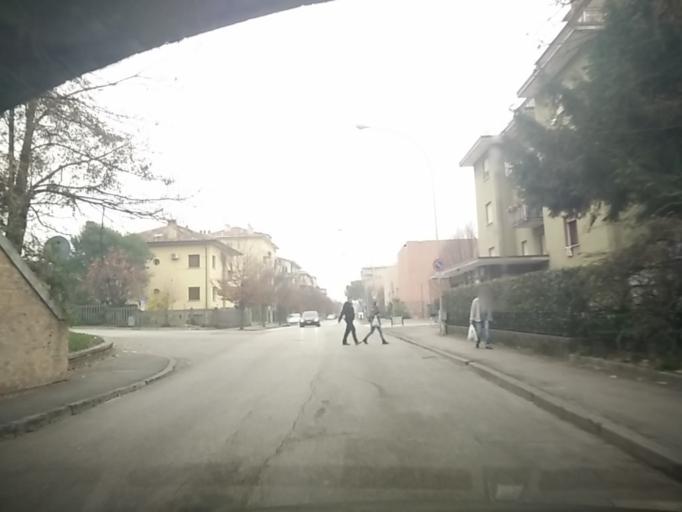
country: IT
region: Veneto
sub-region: Provincia di Treviso
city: Conegliano
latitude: 45.8867
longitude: 12.3044
